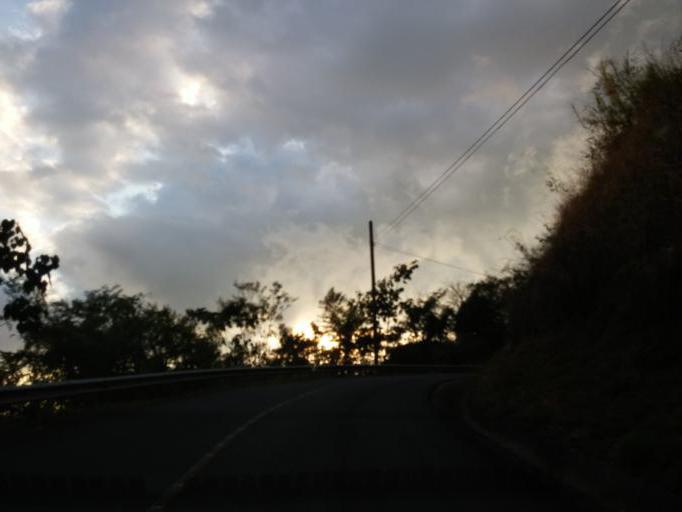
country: CR
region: San Jose
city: Palmichal
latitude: 9.8277
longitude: -84.1961
